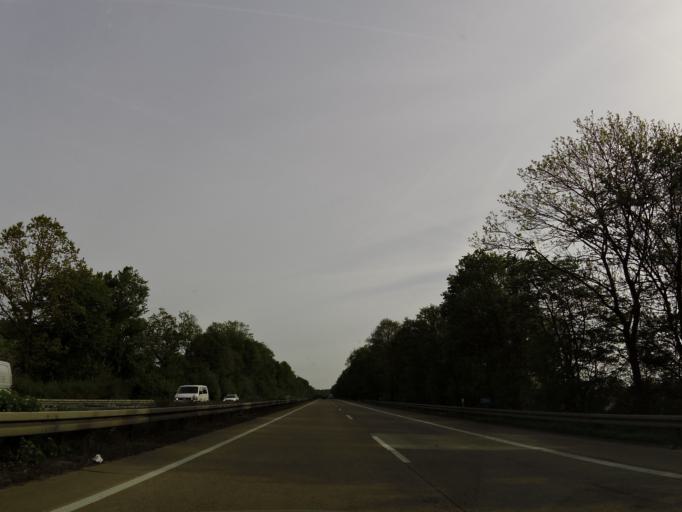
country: DE
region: Lower Saxony
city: Northeim
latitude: 51.7490
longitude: 10.0095
